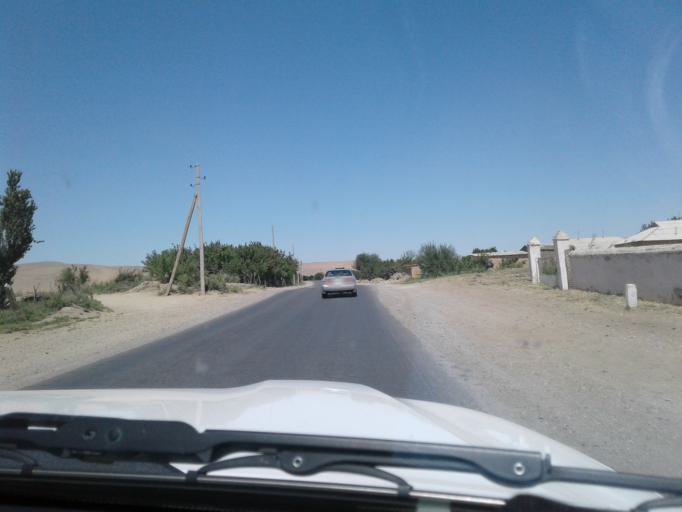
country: AF
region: Badghis
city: Bala Murghab
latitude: 35.9501
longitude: 62.8749
